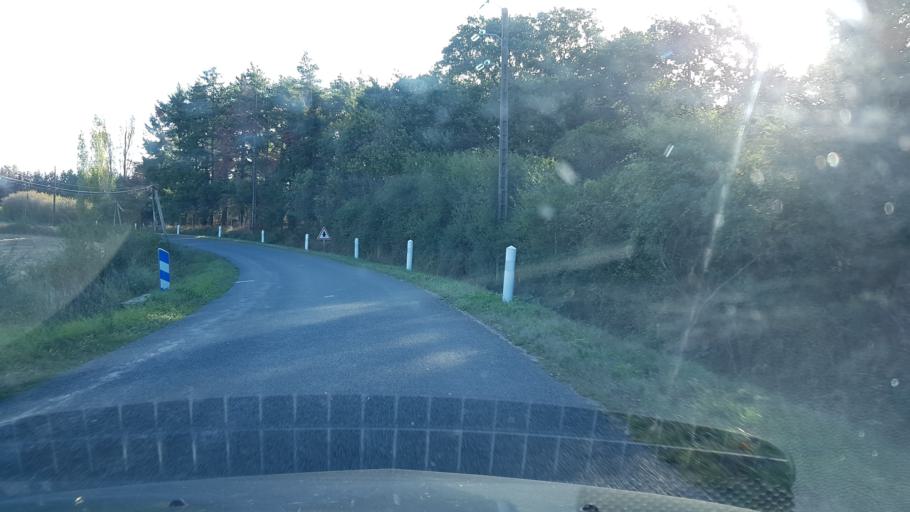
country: FR
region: Centre
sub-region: Departement du Loiret
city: Coullons
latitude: 47.6853
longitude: 2.4596
